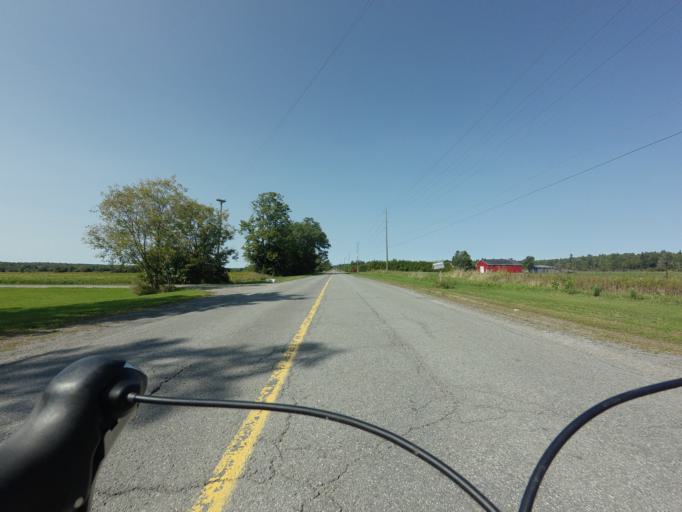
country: CA
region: Ontario
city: Arnprior
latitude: 45.4853
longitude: -76.1291
